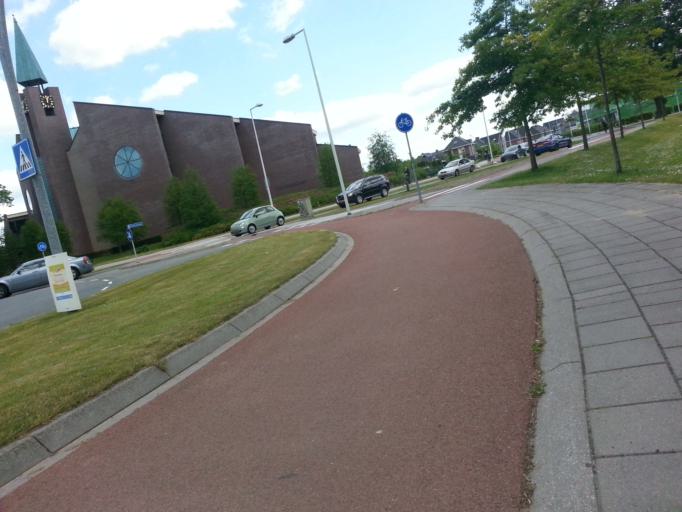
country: NL
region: Gelderland
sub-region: Gemeente Barneveld
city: Barneveld
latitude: 52.1266
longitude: 5.5880
